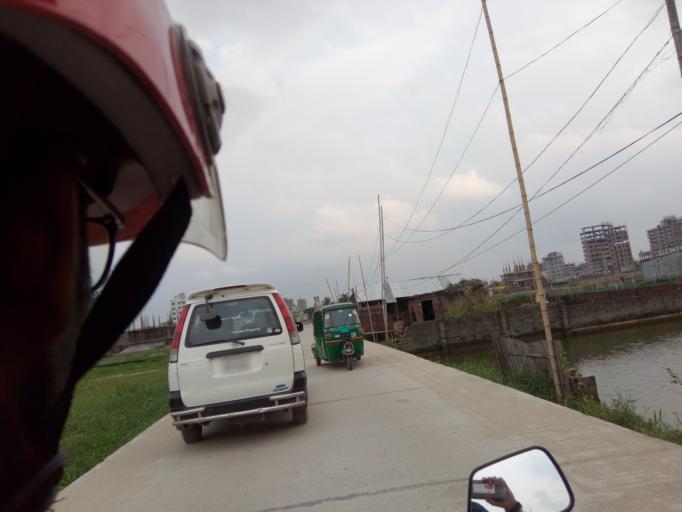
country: BD
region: Dhaka
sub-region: Dhaka
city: Dhaka
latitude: 23.7012
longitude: 90.4751
